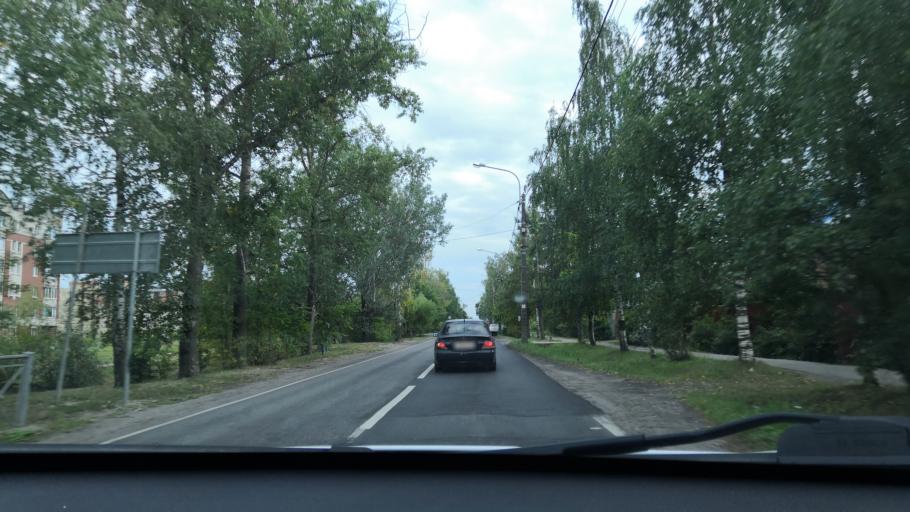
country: RU
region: St.-Petersburg
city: Pushkin
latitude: 59.6988
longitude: 30.4102
